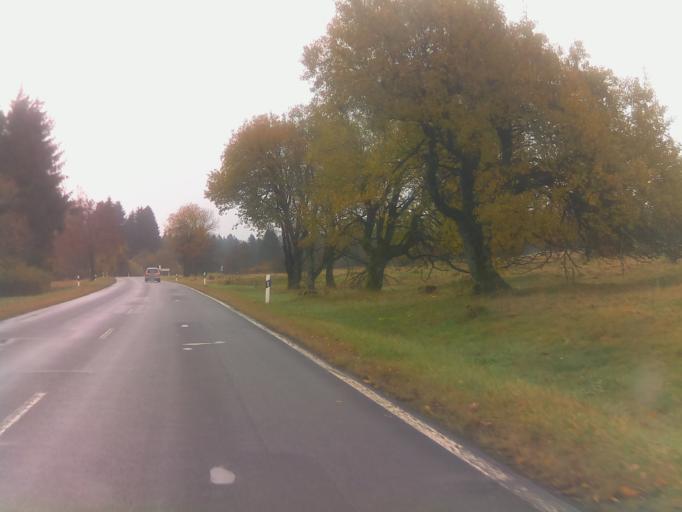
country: DE
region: Hesse
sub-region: Regierungsbezirk Giessen
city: Ulrichstein
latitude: 50.5145
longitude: 9.2213
